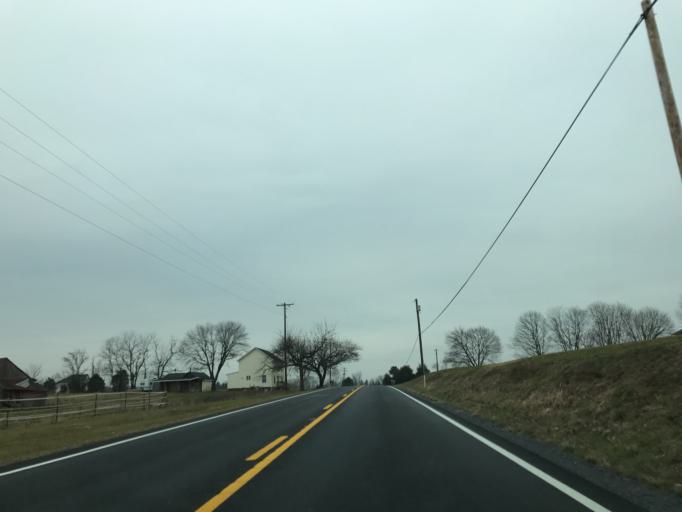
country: US
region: Maryland
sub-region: Frederick County
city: Emmitsburg
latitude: 39.6836
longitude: -77.2527
